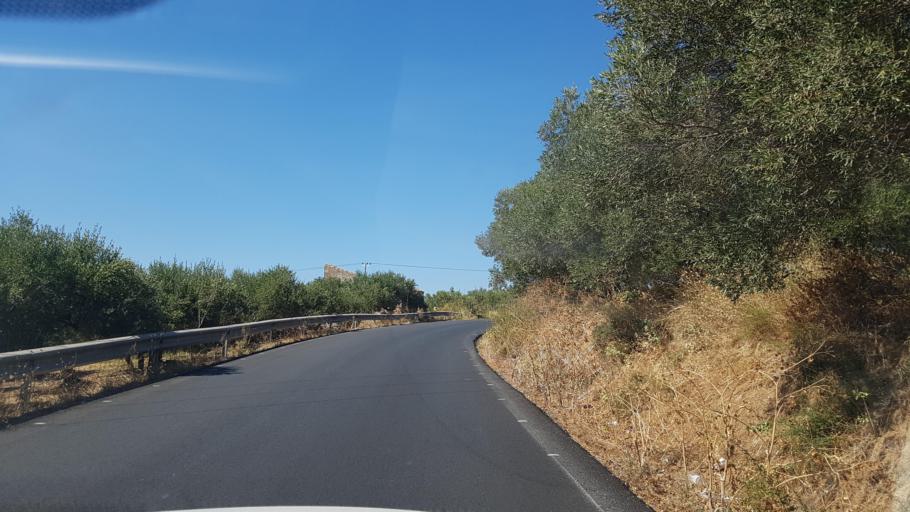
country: GR
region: Crete
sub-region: Nomos Chanias
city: Kissamos
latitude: 35.4897
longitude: 23.6917
